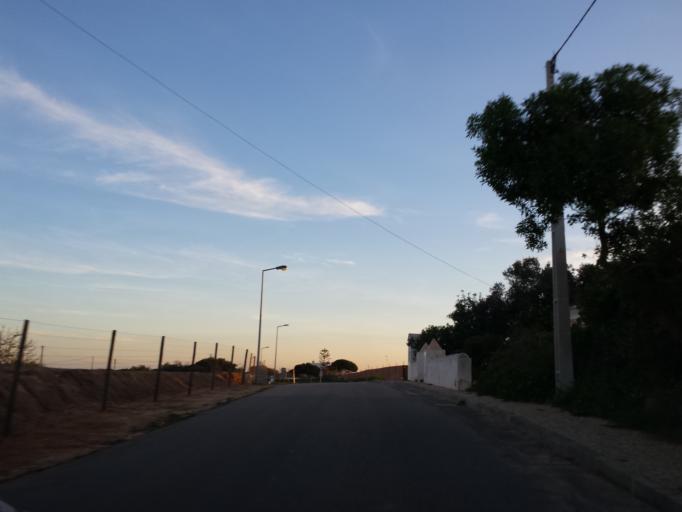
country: PT
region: Faro
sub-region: Lagos
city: Lagos
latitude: 37.0882
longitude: -8.6715
